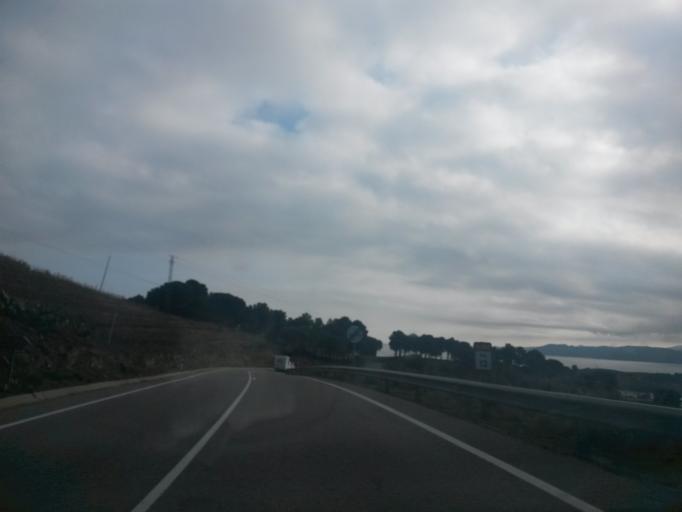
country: ES
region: Catalonia
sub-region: Provincia de Girona
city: Colera
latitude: 42.3990
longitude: 3.1506
